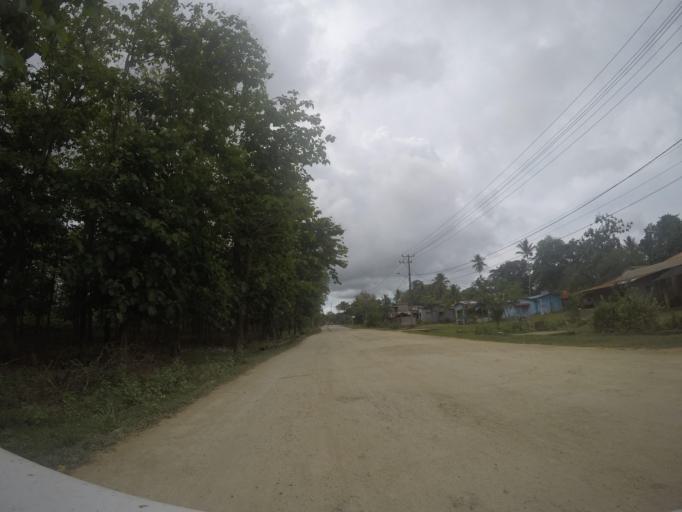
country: TL
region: Lautem
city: Lospalos
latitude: -8.5145
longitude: 126.9878
